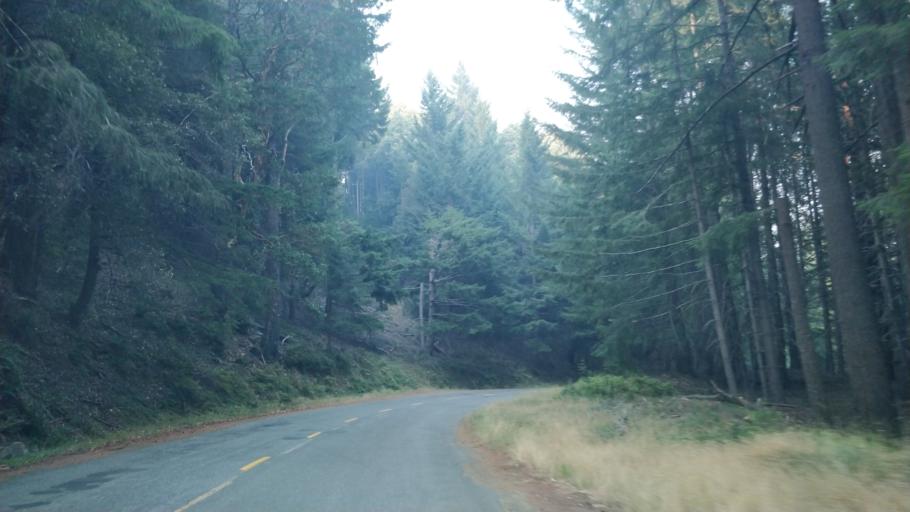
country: US
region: California
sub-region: Humboldt County
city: Rio Dell
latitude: 40.2992
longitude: -124.0568
